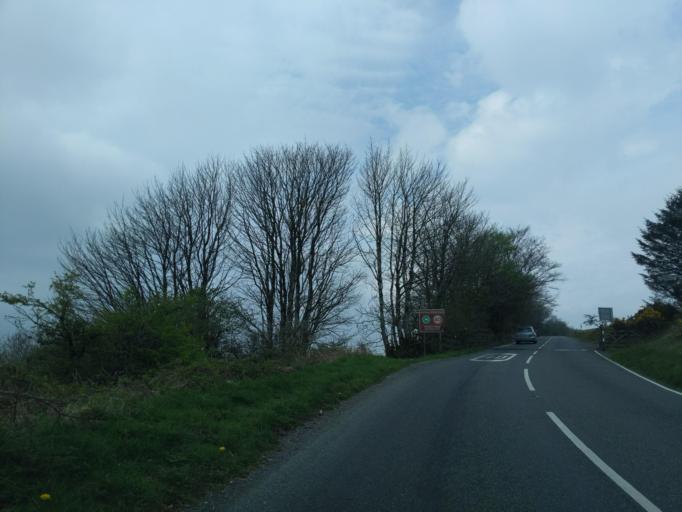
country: GB
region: England
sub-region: Devon
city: Yelverton
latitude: 50.5104
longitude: -4.0447
